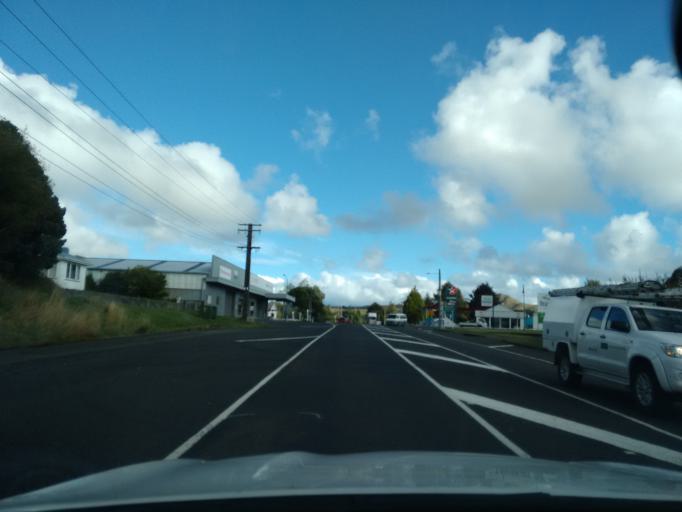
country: NZ
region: Manawatu-Wanganui
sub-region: Ruapehu District
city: Waiouru
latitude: -39.4268
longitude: 175.2819
